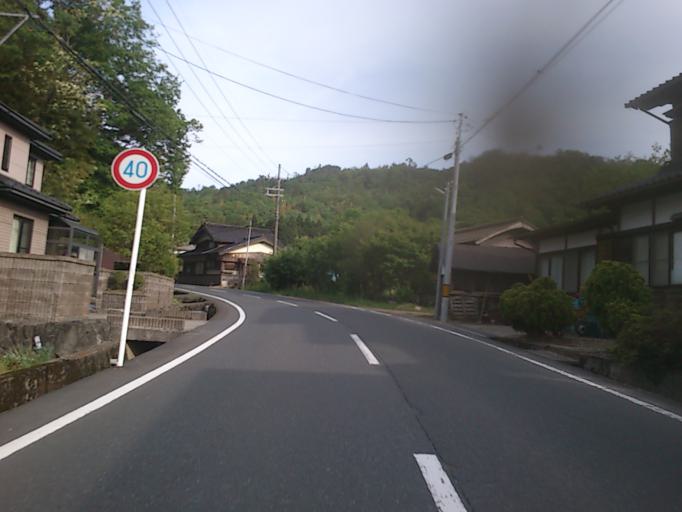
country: JP
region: Kyoto
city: Miyazu
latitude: 35.5759
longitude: 135.1018
